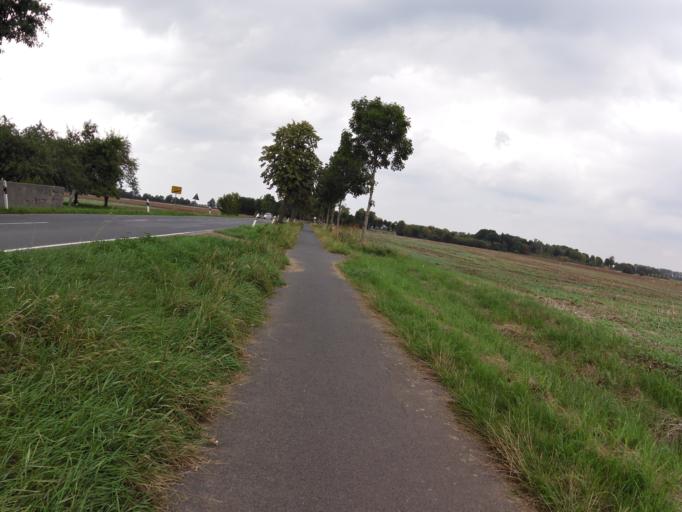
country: DE
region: Lower Saxony
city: Blender
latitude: 52.9148
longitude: 9.1603
